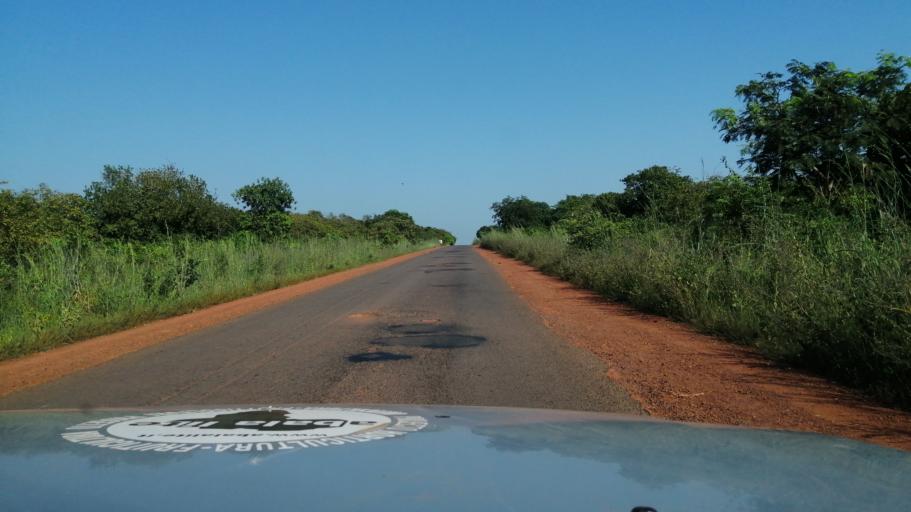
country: GW
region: Bissau
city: Bissau
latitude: 11.9588
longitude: -15.5243
